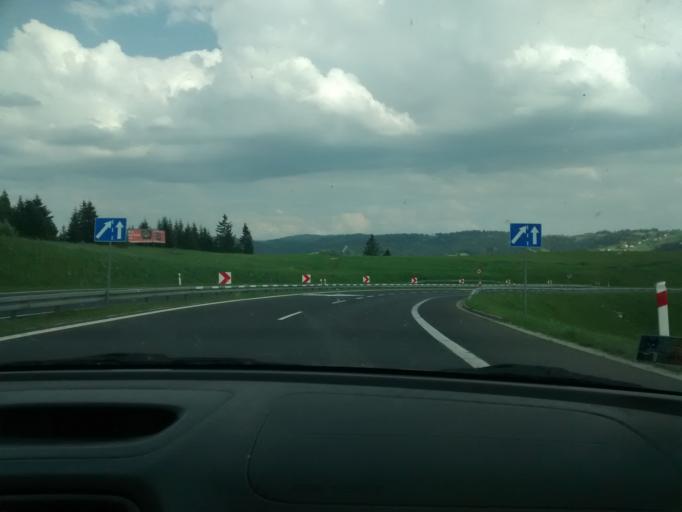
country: PL
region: Lesser Poland Voivodeship
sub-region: Powiat nowotarski
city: Rokiciny
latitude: 49.5740
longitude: 19.9467
